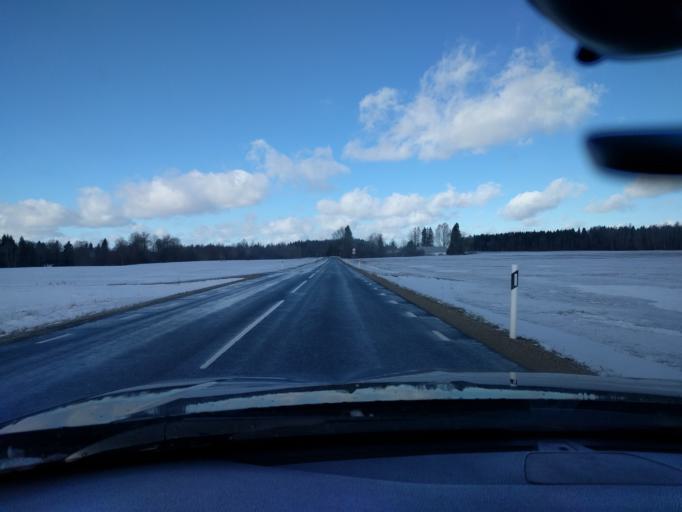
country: EE
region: Harju
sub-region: Anija vald
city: Kehra
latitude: 59.2803
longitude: 25.2720
